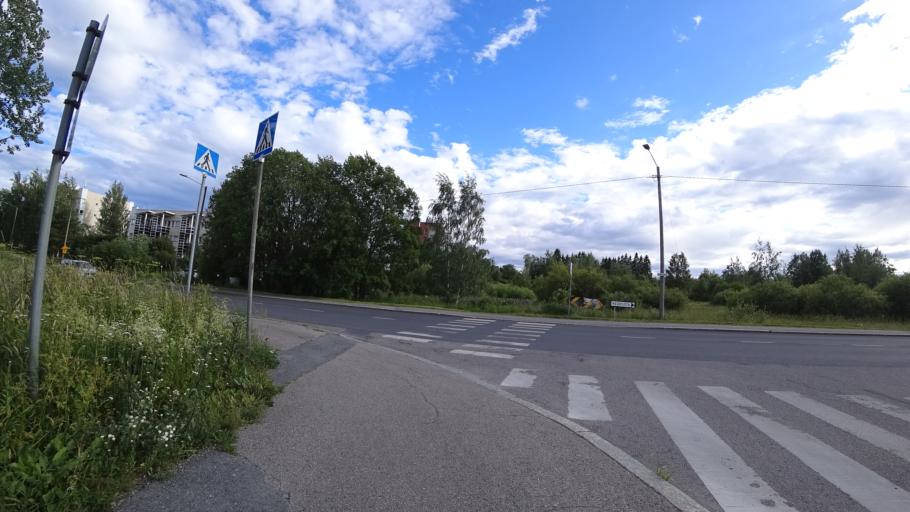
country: FI
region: Pirkanmaa
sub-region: Tampere
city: Pirkkala
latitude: 61.5030
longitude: 23.6859
